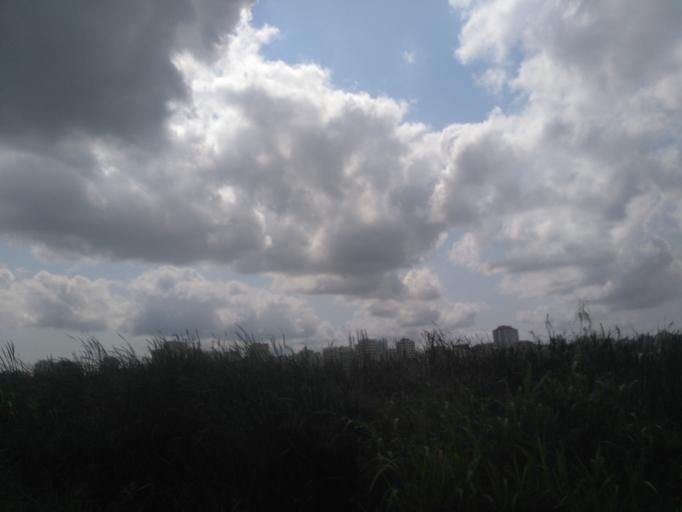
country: TZ
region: Dar es Salaam
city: Dar es Salaam
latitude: -6.8128
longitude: 39.2668
